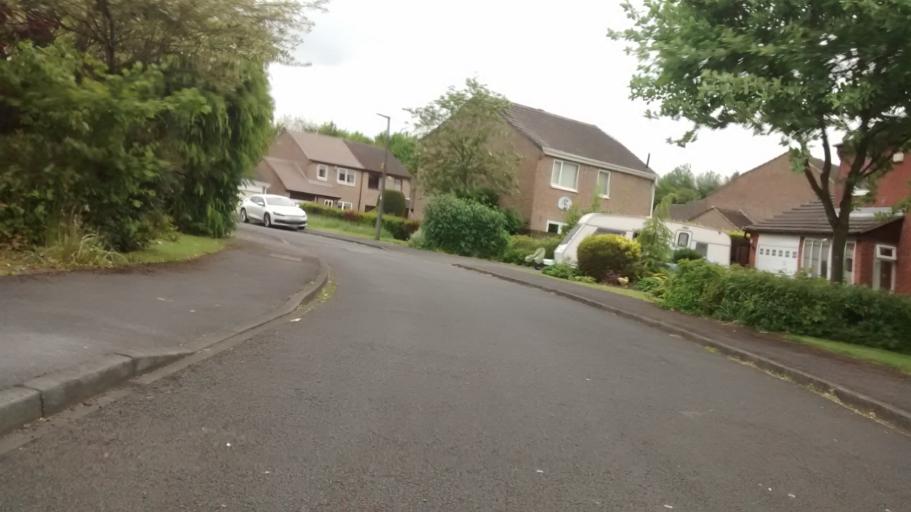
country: GB
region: England
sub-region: County Durham
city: Pittington
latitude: 54.7924
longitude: -1.4929
